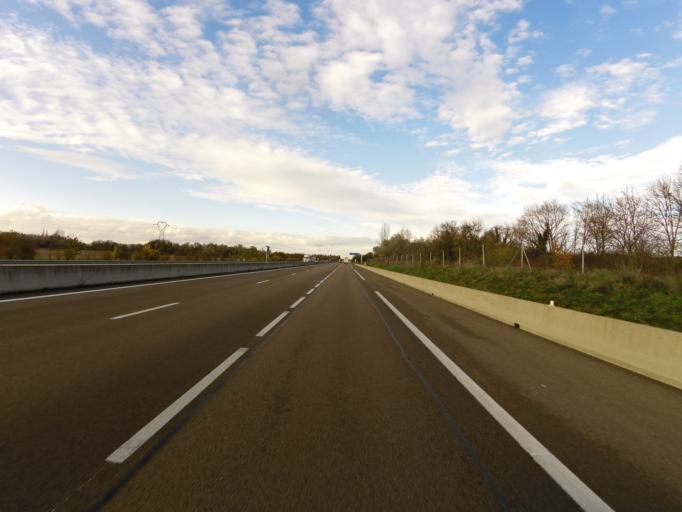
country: FR
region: Bourgogne
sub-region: Departement de la Cote-d'Or
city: Couternon
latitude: 47.3143
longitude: 5.1724
